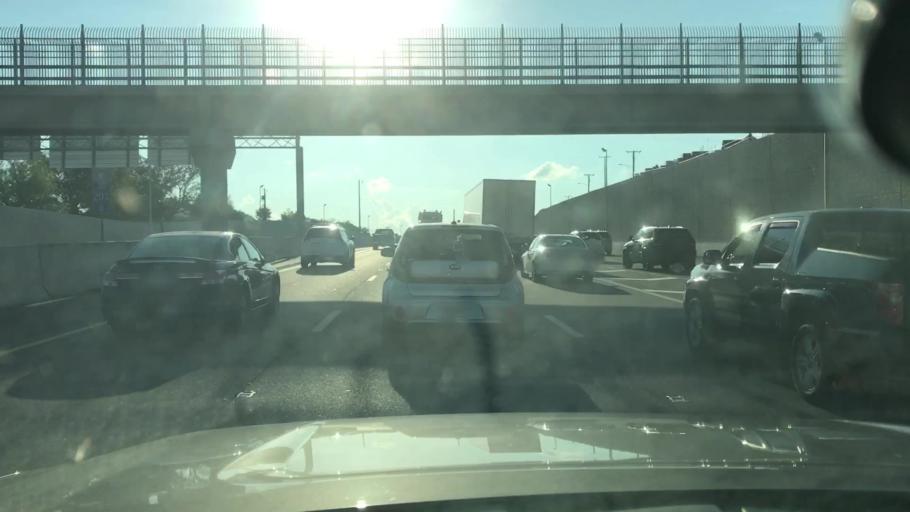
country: US
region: Tennessee
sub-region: Davidson County
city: Belle Meade
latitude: 36.1530
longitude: -86.8637
